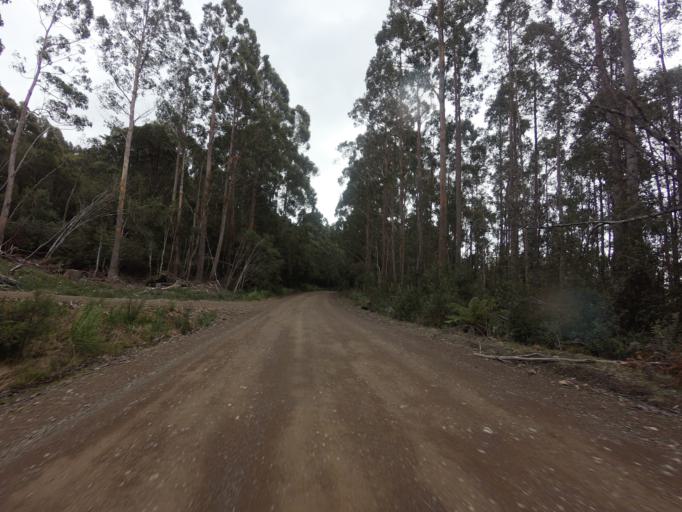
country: AU
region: Tasmania
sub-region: Huon Valley
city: Geeveston
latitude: -43.4859
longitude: 146.8913
